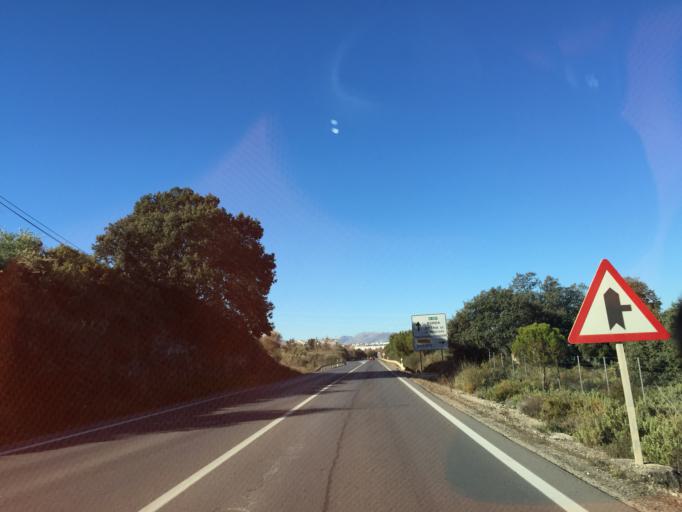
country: ES
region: Andalusia
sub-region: Provincia de Malaga
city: Ronda
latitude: 36.7576
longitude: -5.1424
